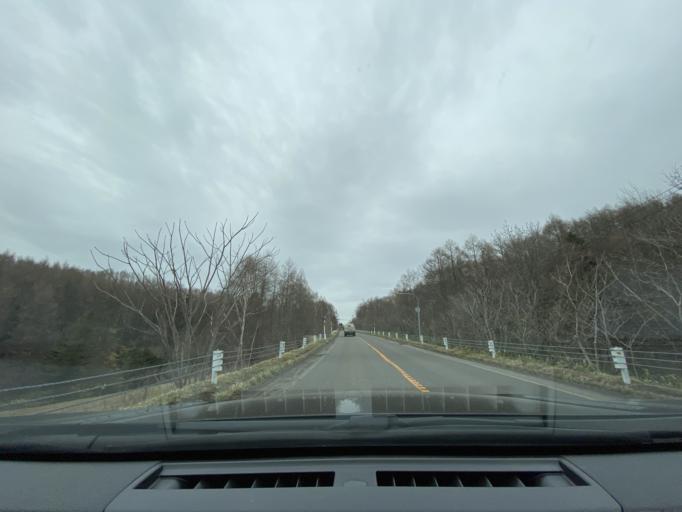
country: JP
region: Hokkaido
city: Nayoro
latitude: 44.0890
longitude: 142.4591
